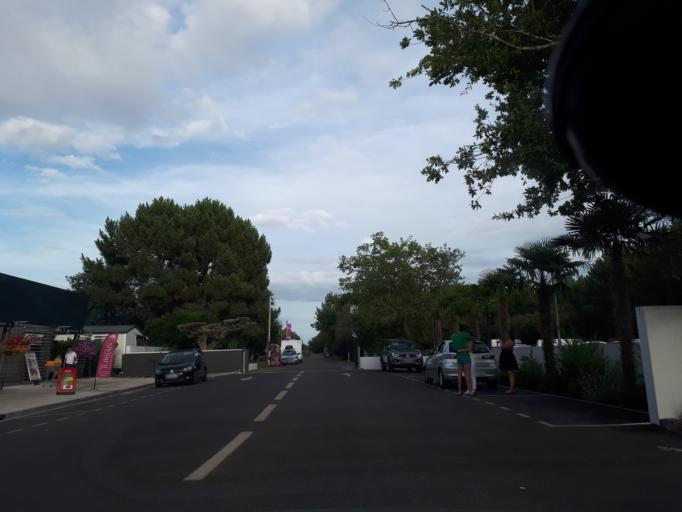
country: FR
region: Aquitaine
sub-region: Departement des Landes
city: Sanguinet
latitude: 44.4603
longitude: -1.1304
